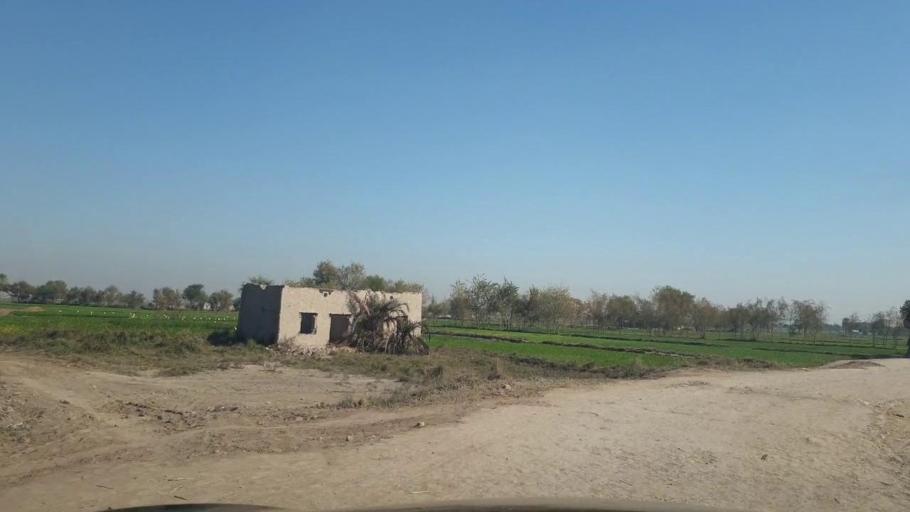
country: PK
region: Sindh
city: Ghotki
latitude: 27.9998
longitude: 69.3571
